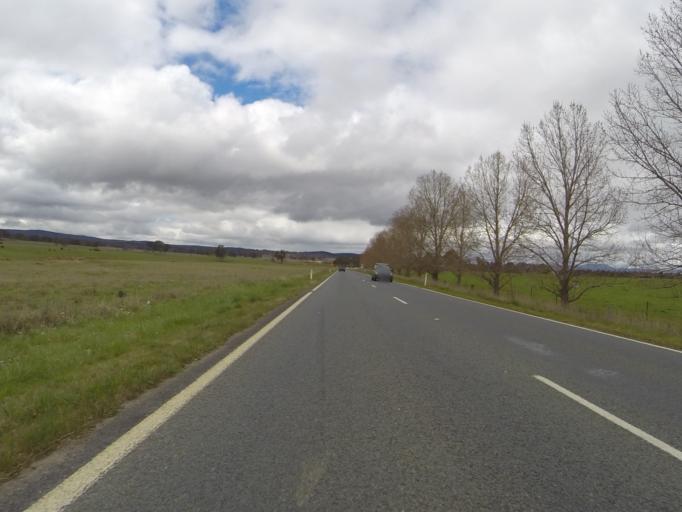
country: AU
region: Australian Capital Territory
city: Canberra
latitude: -35.2612
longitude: 149.1929
